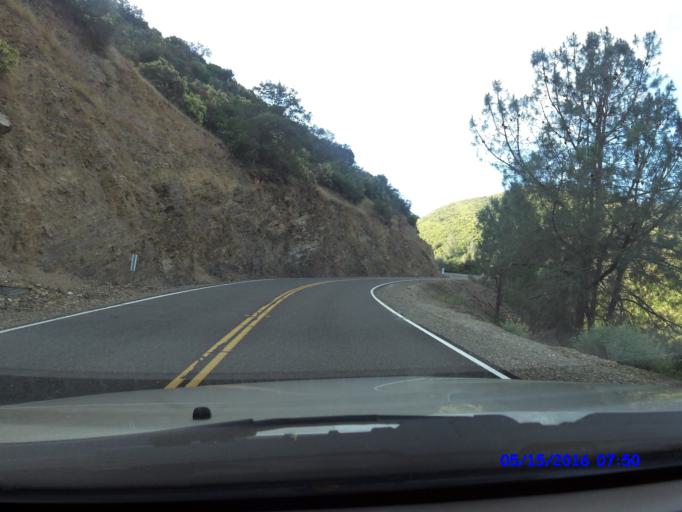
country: US
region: California
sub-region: Mariposa County
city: Mariposa
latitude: 37.5998
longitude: -120.1326
